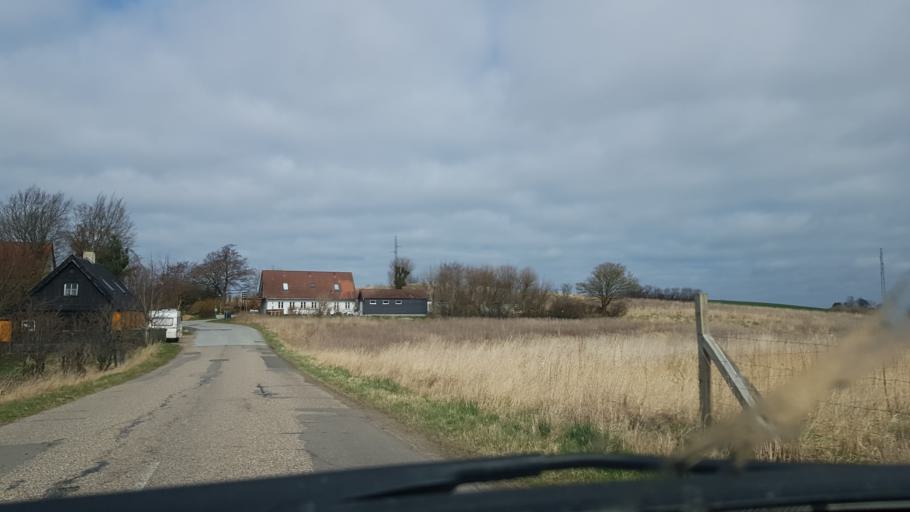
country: DK
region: Zealand
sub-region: Odsherred Kommune
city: Hojby
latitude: 55.9195
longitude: 11.5683
